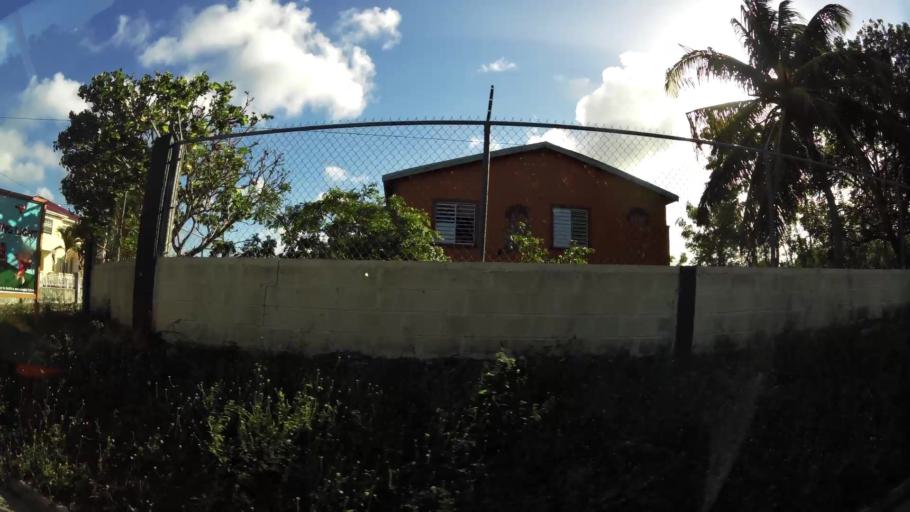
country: AG
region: Saint John
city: Potters Village
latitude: 17.0934
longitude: -61.8010
